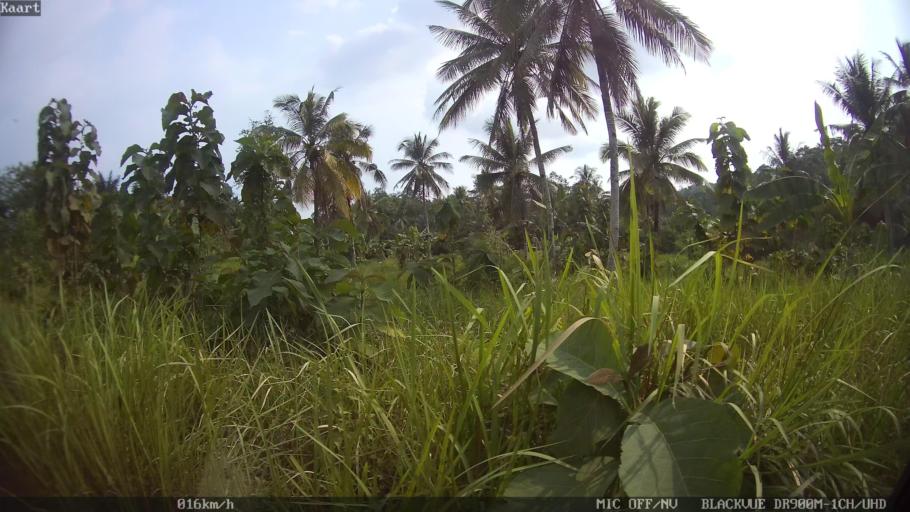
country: ID
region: Lampung
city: Gadingrejo
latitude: -5.3964
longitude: 105.0231
